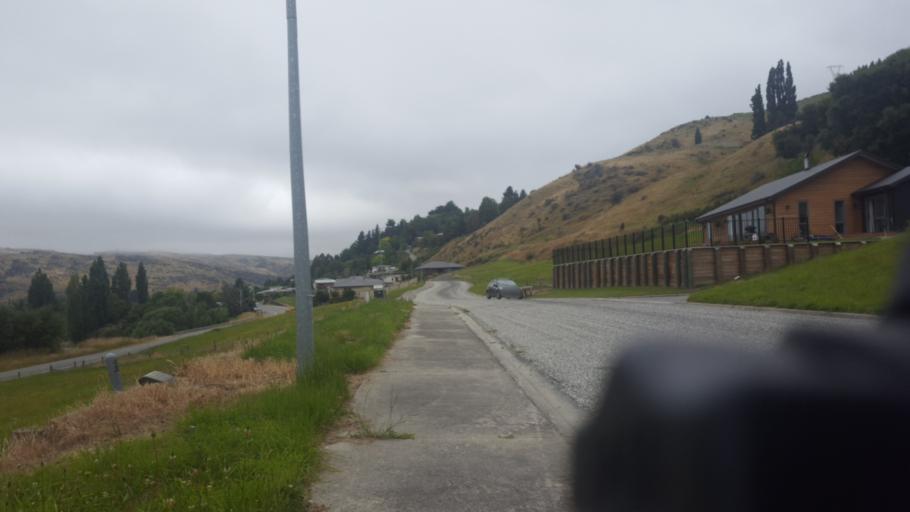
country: NZ
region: Otago
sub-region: Queenstown-Lakes District
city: Kingston
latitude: -45.5327
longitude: 169.2992
